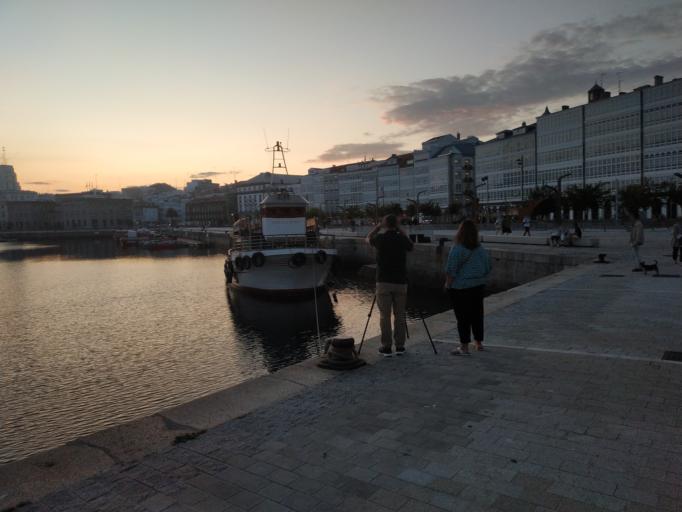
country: ES
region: Galicia
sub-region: Provincia da Coruna
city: A Coruna
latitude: 43.3694
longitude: -8.3957
